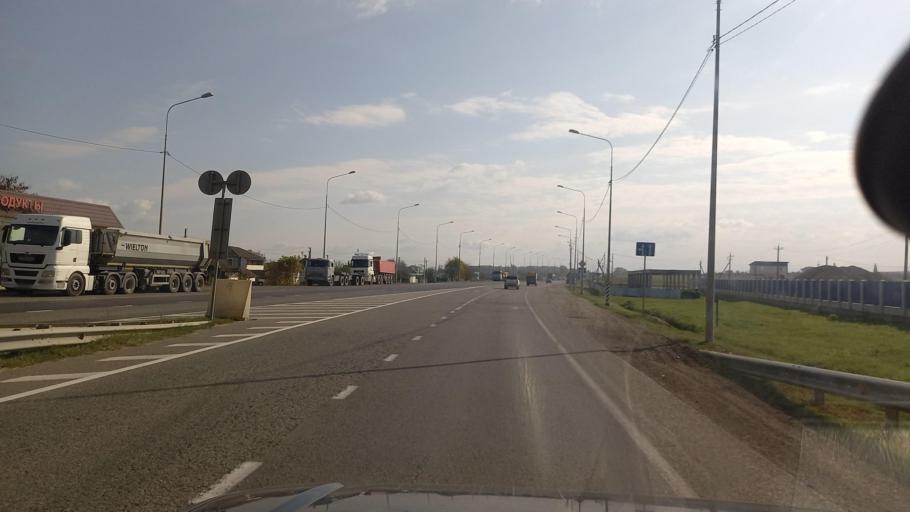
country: RU
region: Krasnodarskiy
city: Novoukrainskiy
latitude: 44.8946
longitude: 38.0606
